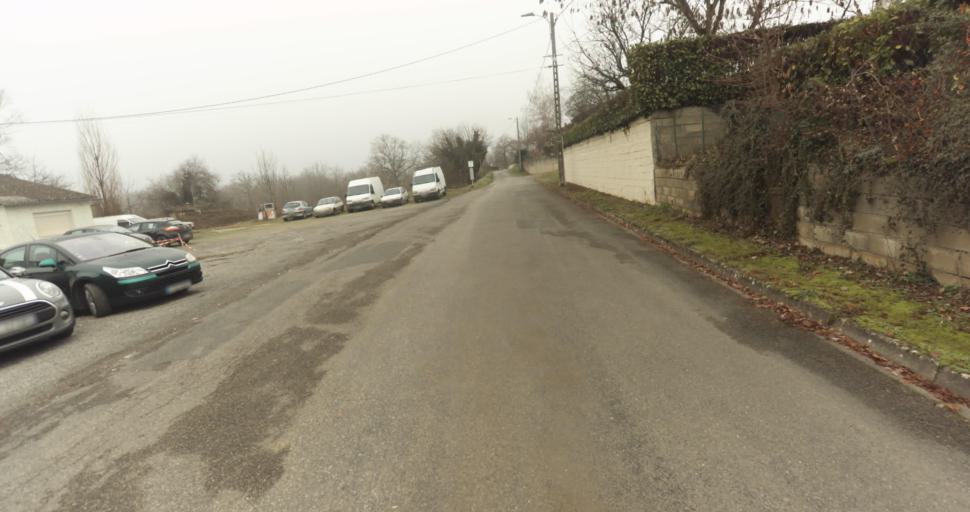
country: FR
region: Midi-Pyrenees
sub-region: Departement du Lot
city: Figeac
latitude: 44.6202
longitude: 2.0365
